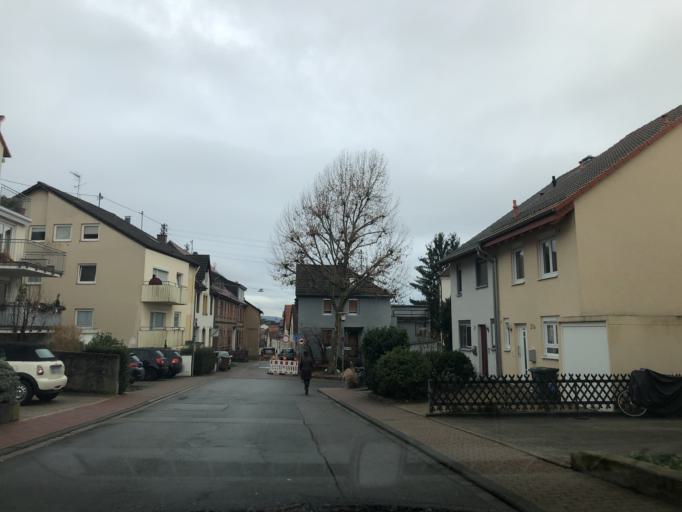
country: DE
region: Baden-Wuerttemberg
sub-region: Karlsruhe Region
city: Dossenheim
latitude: 49.4541
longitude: 8.6757
